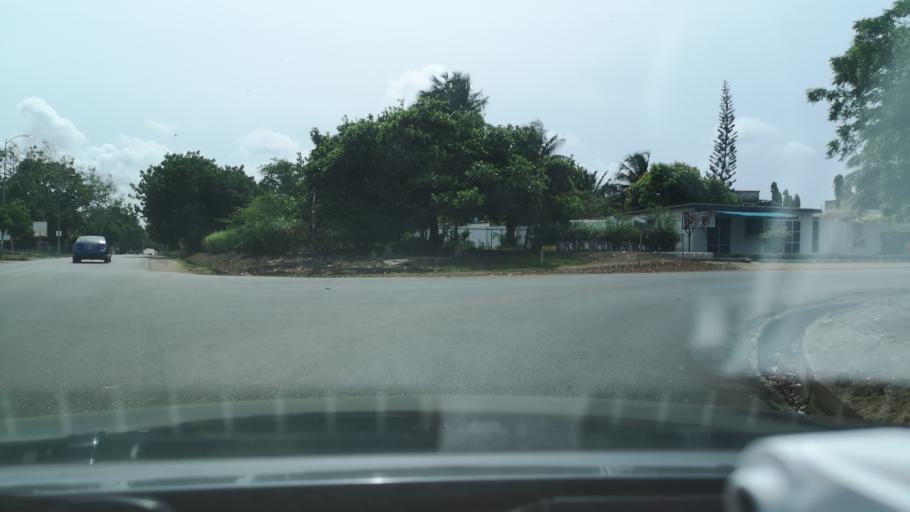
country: GH
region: Greater Accra
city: Tema
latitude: 5.6606
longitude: -0.0254
